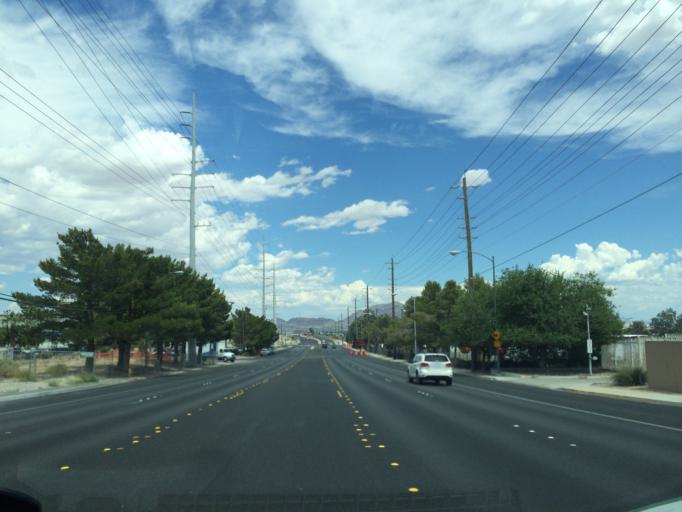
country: US
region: Nevada
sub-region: Clark County
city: North Las Vegas
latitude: 36.2030
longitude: -115.1418
